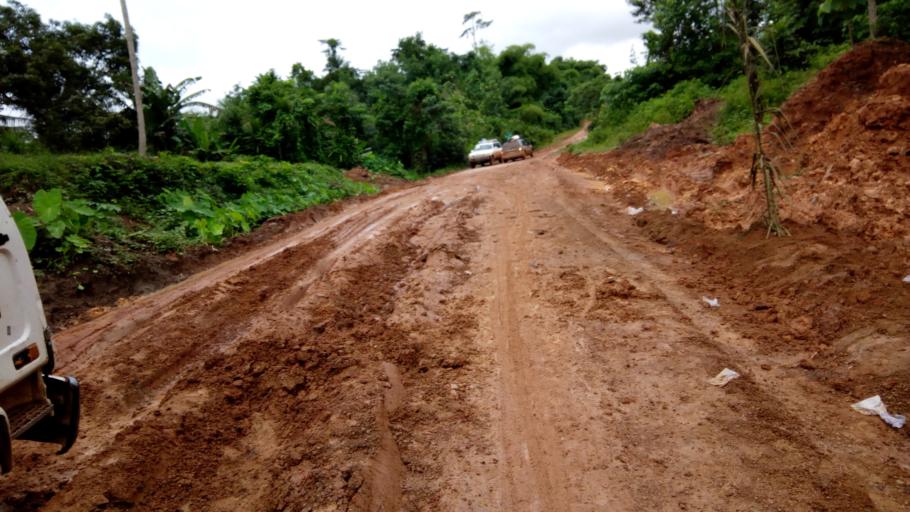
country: CI
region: Dix-Huit Montagnes
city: Toulepleu Guere
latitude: 6.8257
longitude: -8.8108
